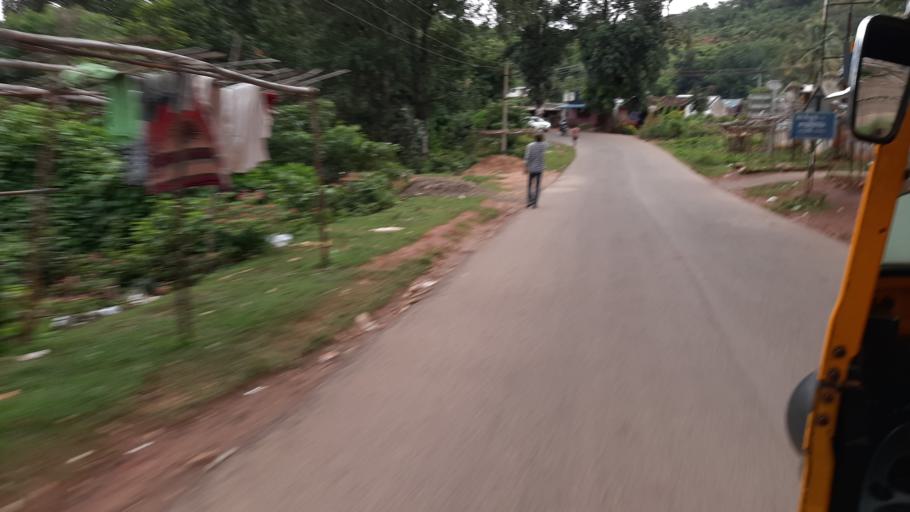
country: IN
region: Andhra Pradesh
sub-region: Vizianagaram District
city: Salur
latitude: 18.2371
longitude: 83.0077
